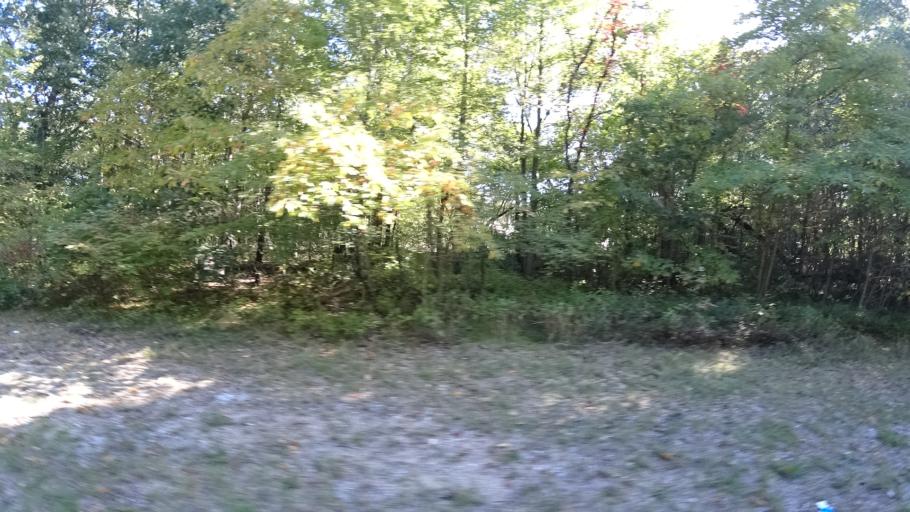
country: US
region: Indiana
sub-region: LaPorte County
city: Michigan City
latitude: 41.6944
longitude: -86.9291
